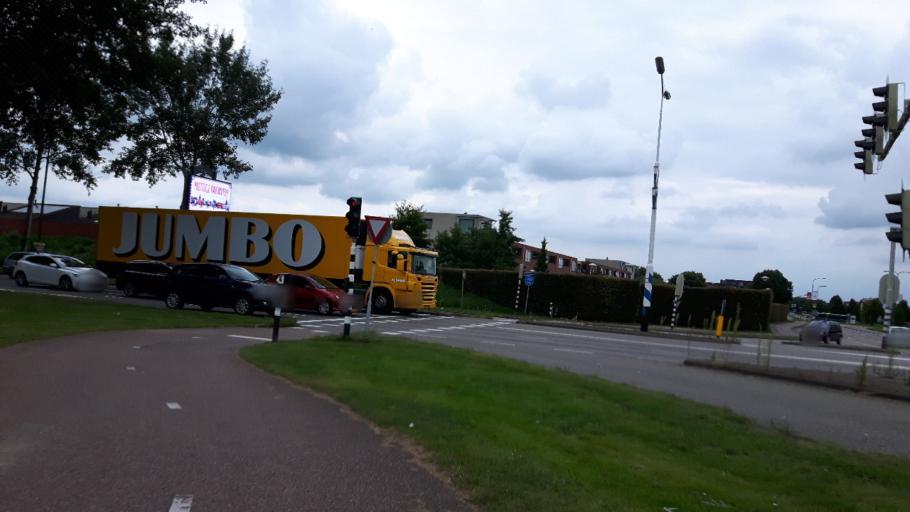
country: NL
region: Utrecht
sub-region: Gemeente Woerden
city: Woerden
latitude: 52.0769
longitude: 4.9005
